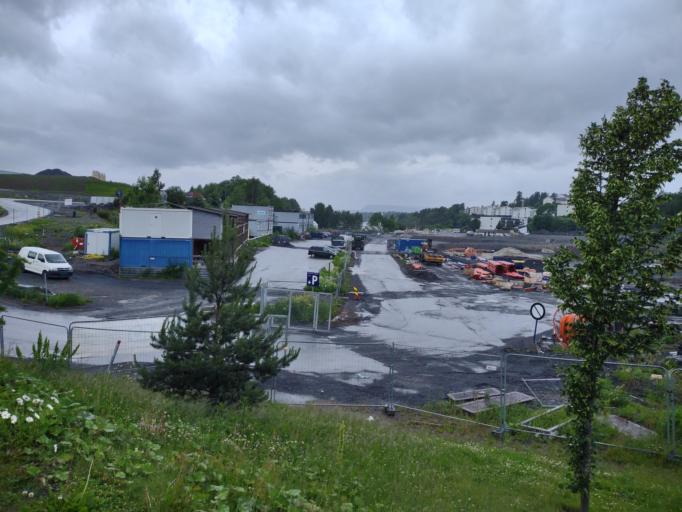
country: NO
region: Akershus
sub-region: Baerum
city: Lysaker
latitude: 59.9052
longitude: 10.6211
